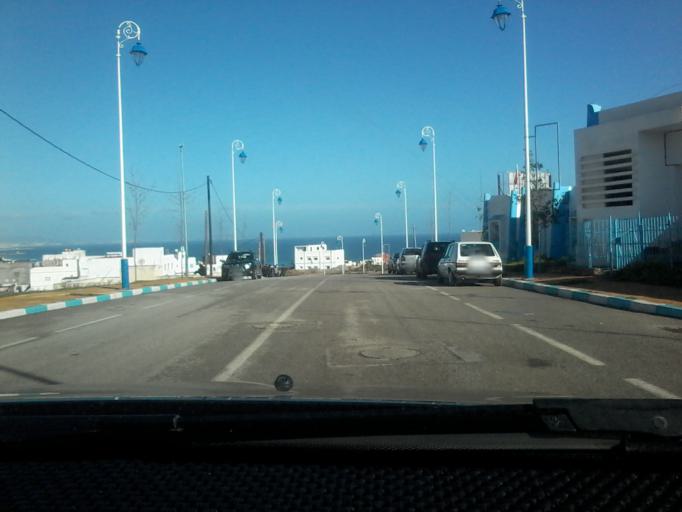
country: MA
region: Tanger-Tetouan
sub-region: Tetouan
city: Martil
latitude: 35.6762
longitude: -5.3259
